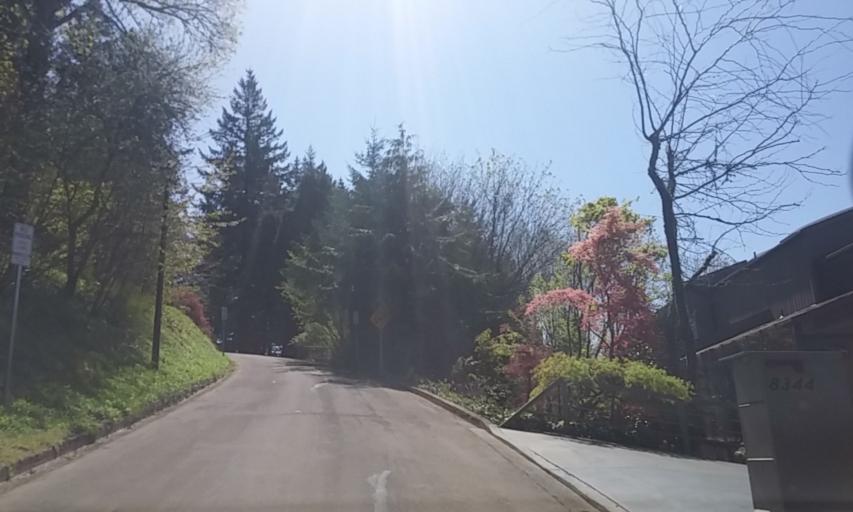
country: US
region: Oregon
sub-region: Washington County
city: West Haven-Sylvan
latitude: 45.5173
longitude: -122.7633
